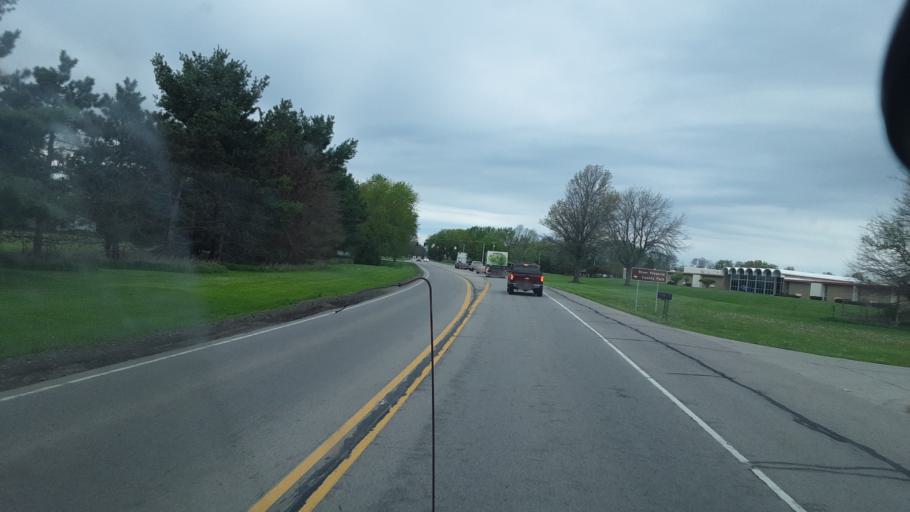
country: US
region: Indiana
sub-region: Elkhart County
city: New Paris
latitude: 41.5159
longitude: -85.7676
